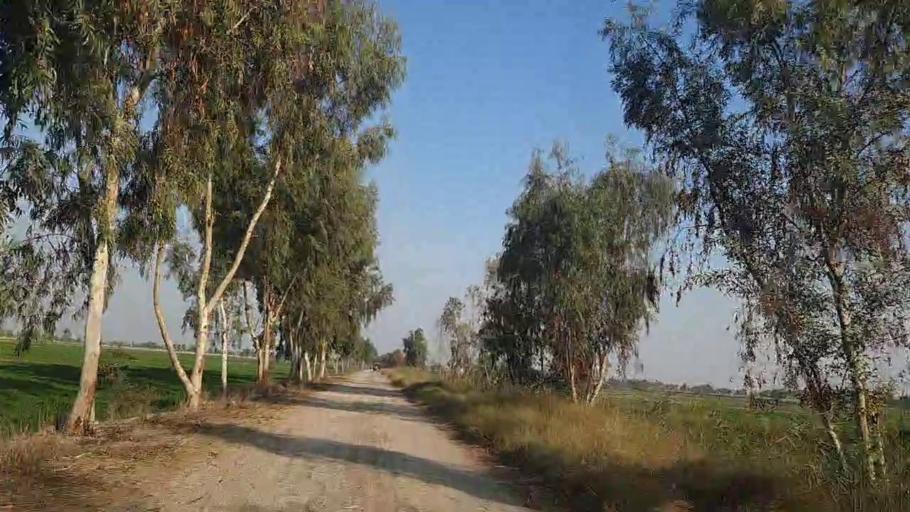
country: PK
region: Sindh
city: Daur
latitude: 26.3401
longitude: 68.1516
